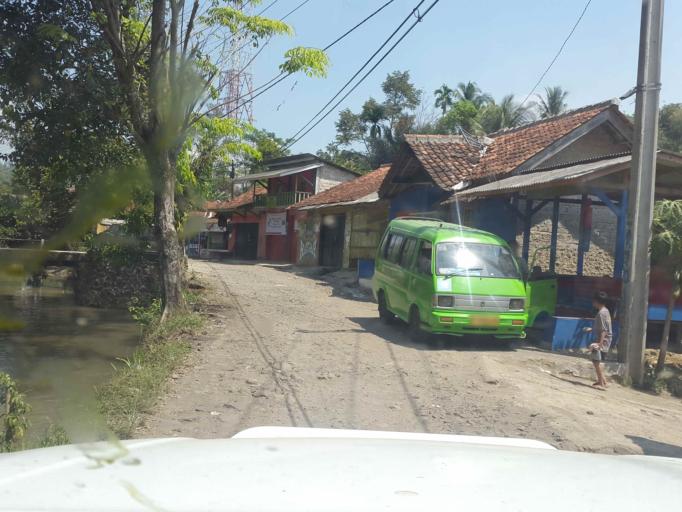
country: ID
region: West Java
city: Ciranjang-hilir
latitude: -6.9006
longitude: 107.2260
